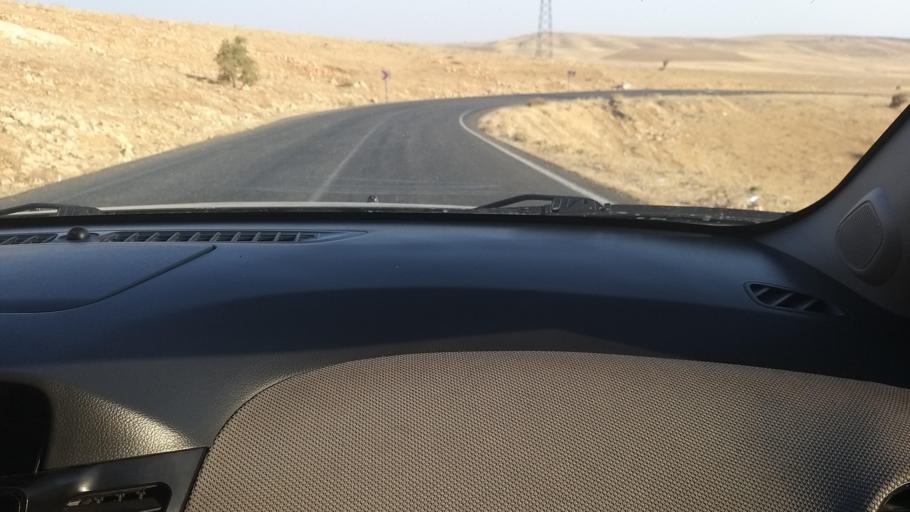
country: TR
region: Diyarbakir
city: Silvan
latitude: 38.1892
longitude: 41.0080
